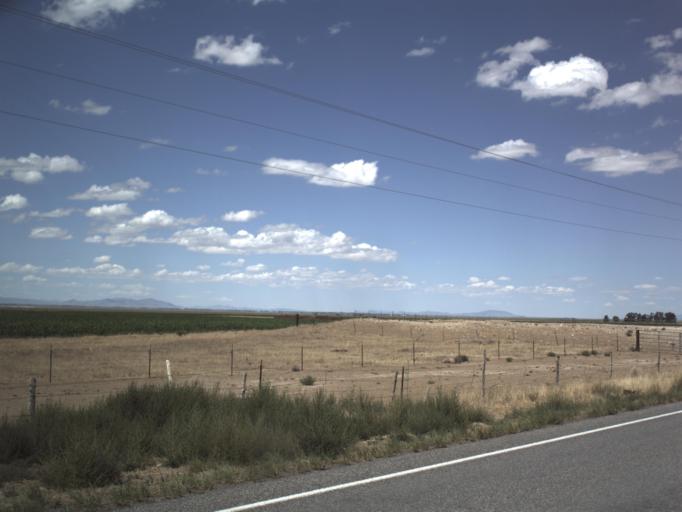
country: US
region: Utah
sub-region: Millard County
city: Fillmore
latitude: 39.1834
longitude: -112.4100
